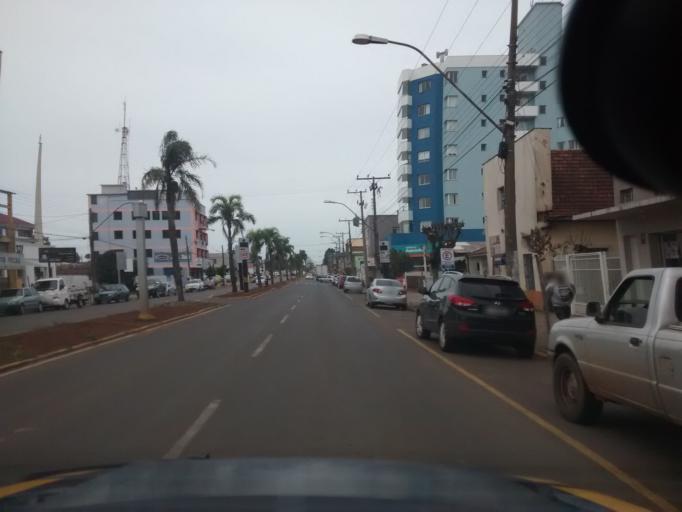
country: BR
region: Rio Grande do Sul
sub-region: Vacaria
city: Vacaria
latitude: -28.5113
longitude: -50.9356
